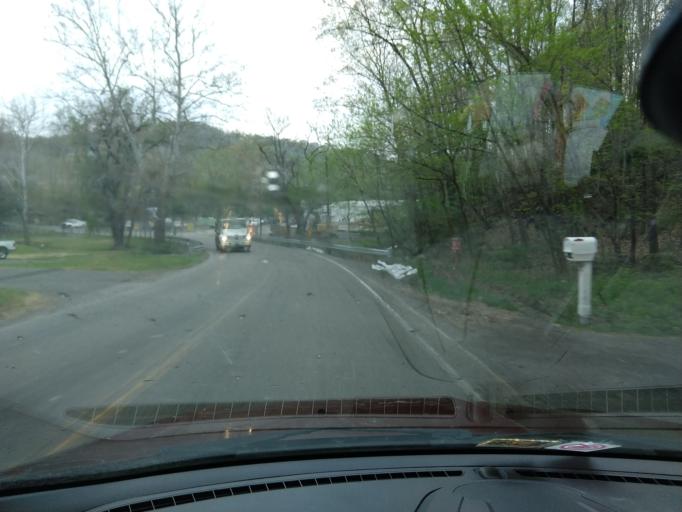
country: US
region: West Virginia
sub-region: Harrison County
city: Despard
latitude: 39.3314
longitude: -80.2894
